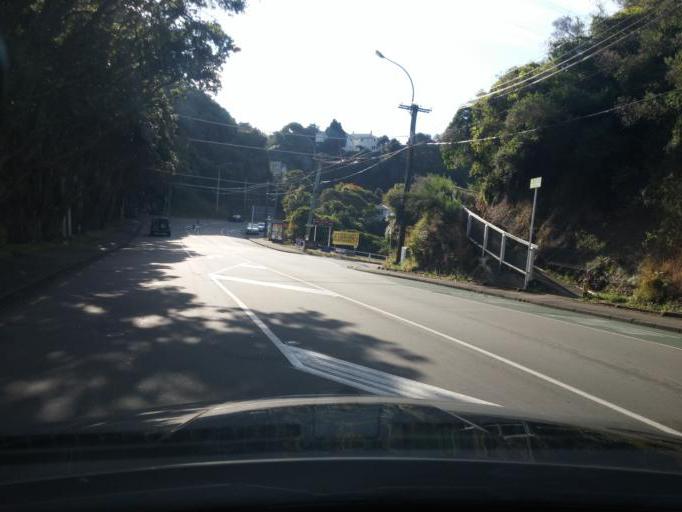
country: NZ
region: Wellington
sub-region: Wellington City
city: Kelburn
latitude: -41.2848
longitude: 174.7540
